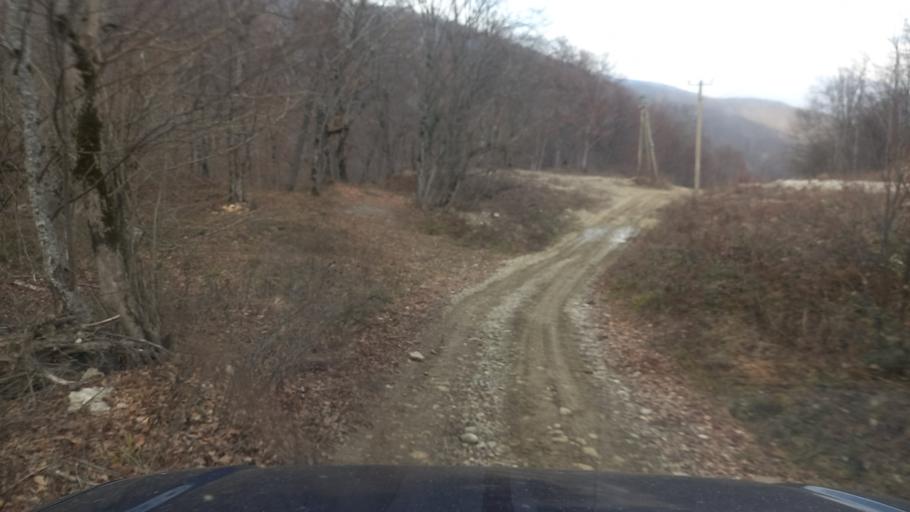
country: RU
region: Krasnodarskiy
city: Neftegorsk
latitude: 44.2129
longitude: 39.7117
